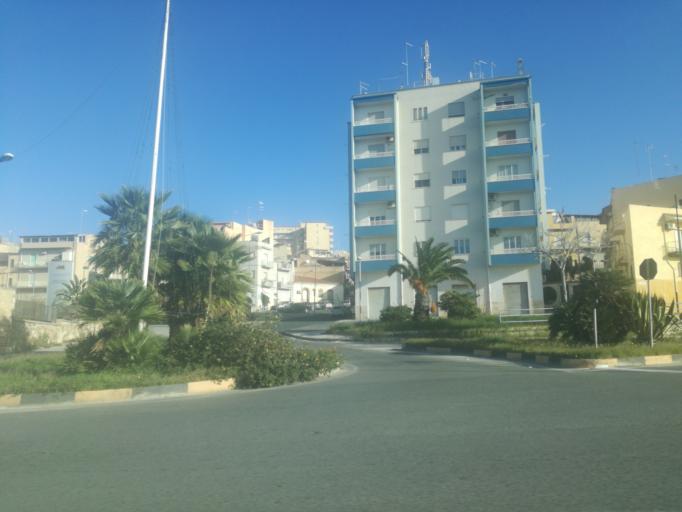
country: IT
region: Sicily
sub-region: Provincia di Caltanissetta
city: Gela
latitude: 37.0621
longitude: 14.2532
